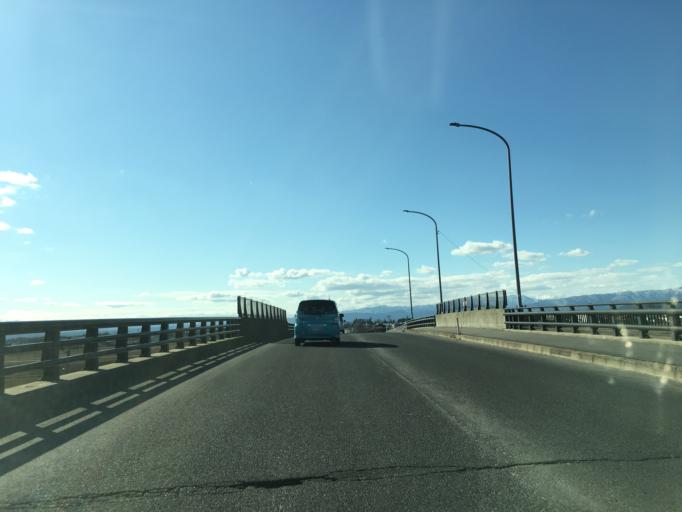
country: JP
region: Yamagata
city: Takahata
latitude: 38.0051
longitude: 140.1540
